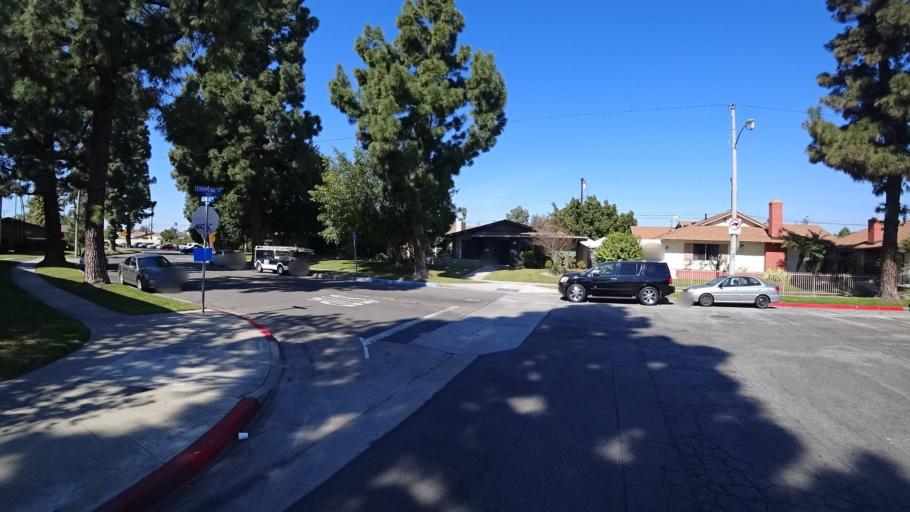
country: US
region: California
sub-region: Orange County
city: Anaheim
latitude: 33.8429
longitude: -117.9473
